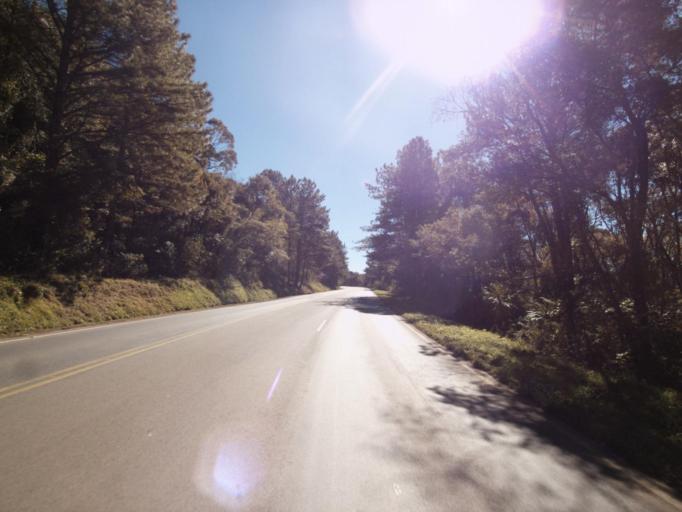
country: BR
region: Santa Catarina
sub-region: Joacaba
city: Joacaba
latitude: -26.9778
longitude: -51.7599
